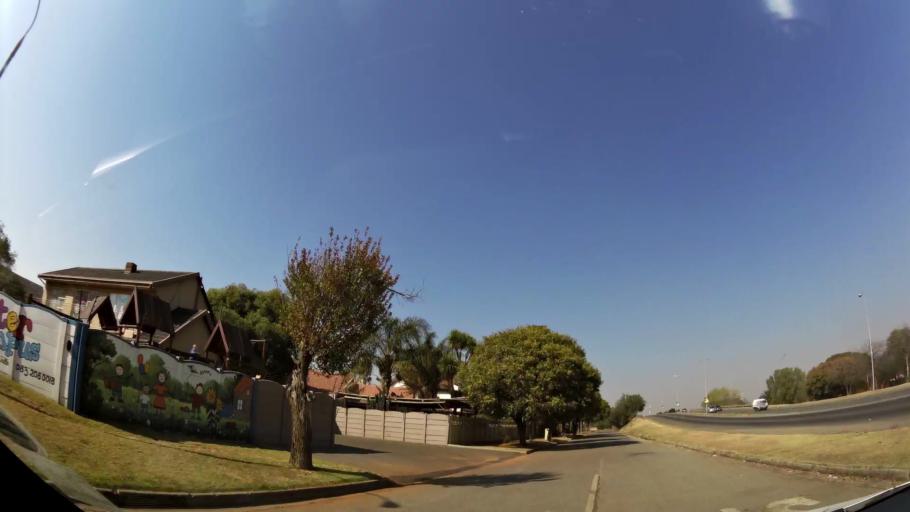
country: ZA
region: Gauteng
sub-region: Ekurhuleni Metropolitan Municipality
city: Boksburg
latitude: -26.2494
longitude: 28.2650
